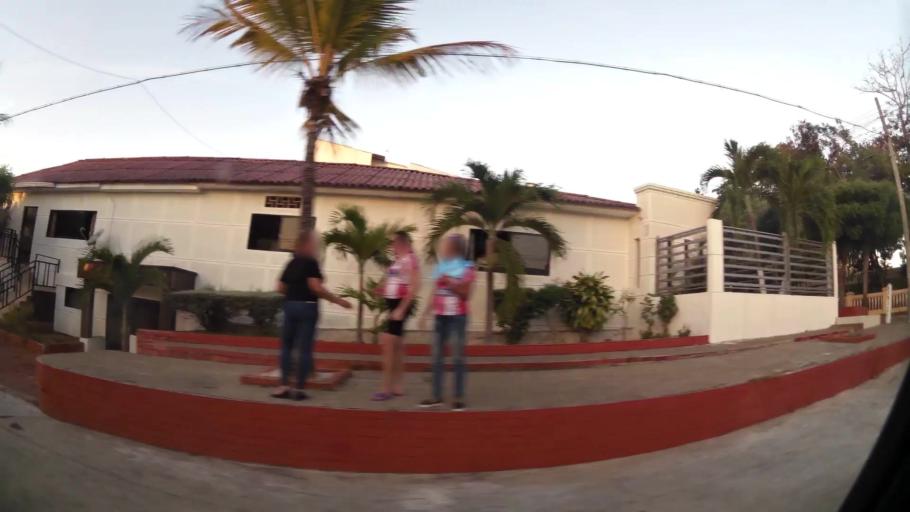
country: CO
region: Atlantico
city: Barranquilla
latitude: 10.9820
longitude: -74.8017
